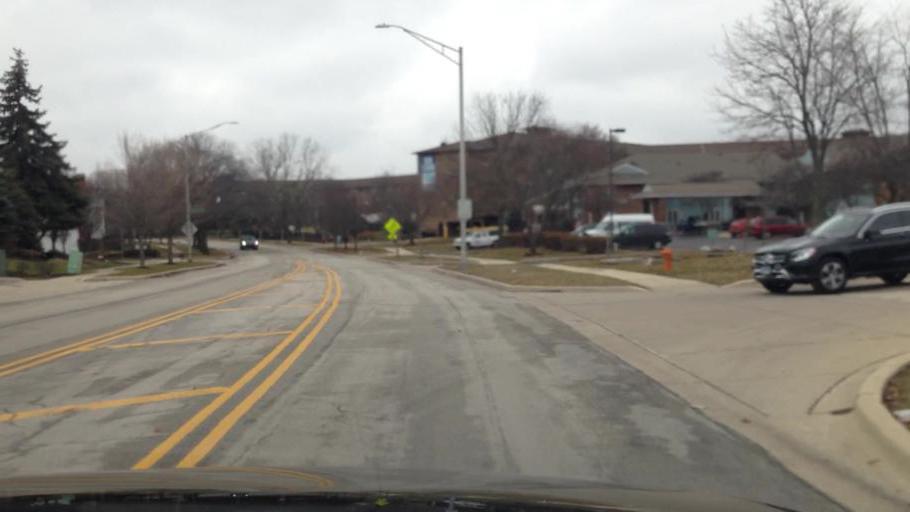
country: US
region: Illinois
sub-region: DuPage County
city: Naperville
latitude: 41.7969
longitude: -88.1269
